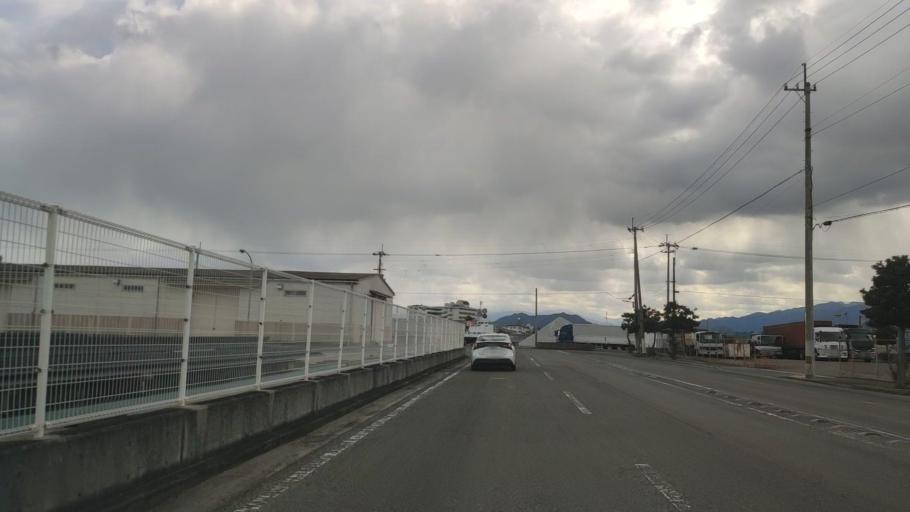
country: JP
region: Ehime
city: Saijo
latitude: 34.0615
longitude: 133.0189
